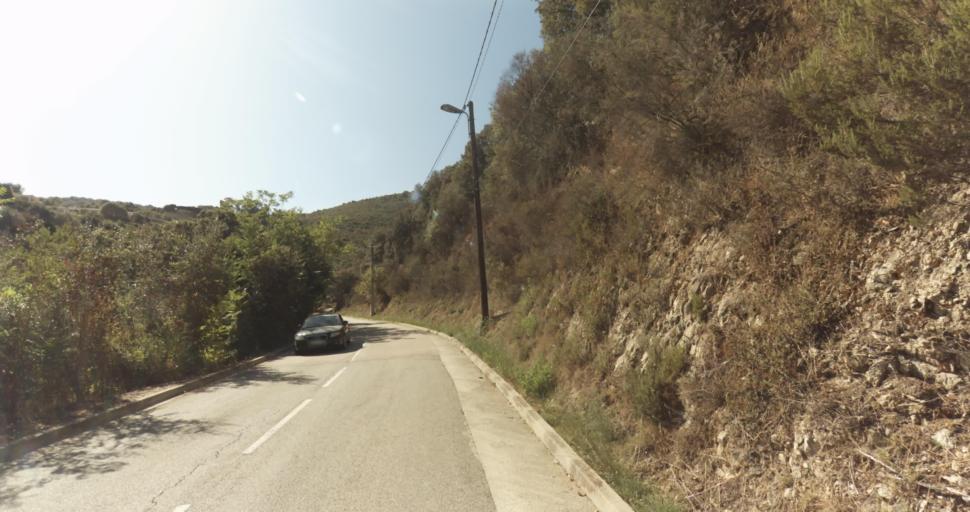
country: FR
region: Corsica
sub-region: Departement de la Corse-du-Sud
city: Ajaccio
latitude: 41.9273
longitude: 8.7065
